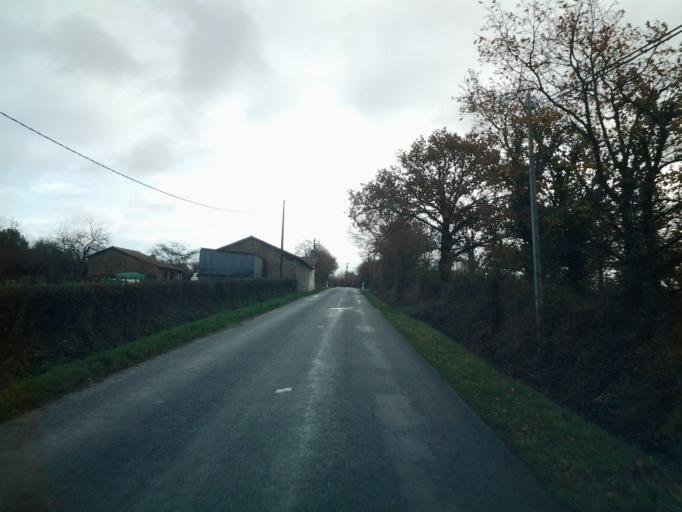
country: FR
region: Pays de la Loire
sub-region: Departement de la Vendee
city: La Roche-sur-Yon
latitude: 46.6503
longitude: -1.3808
